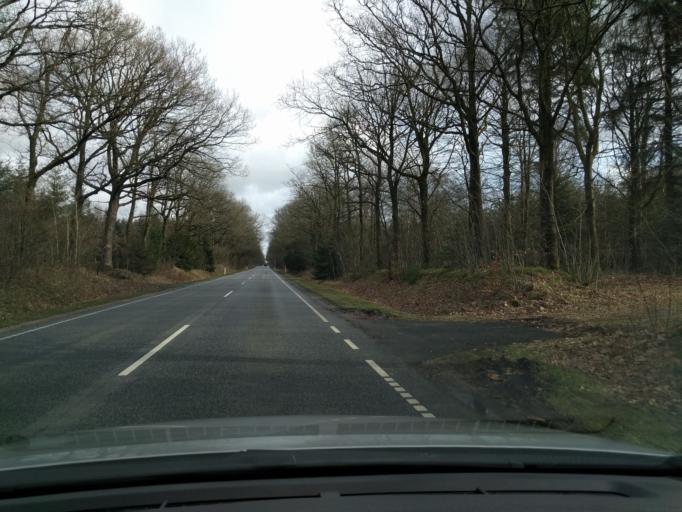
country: DK
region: South Denmark
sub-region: Tonder Kommune
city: Logumkloster
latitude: 55.0612
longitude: 8.9386
